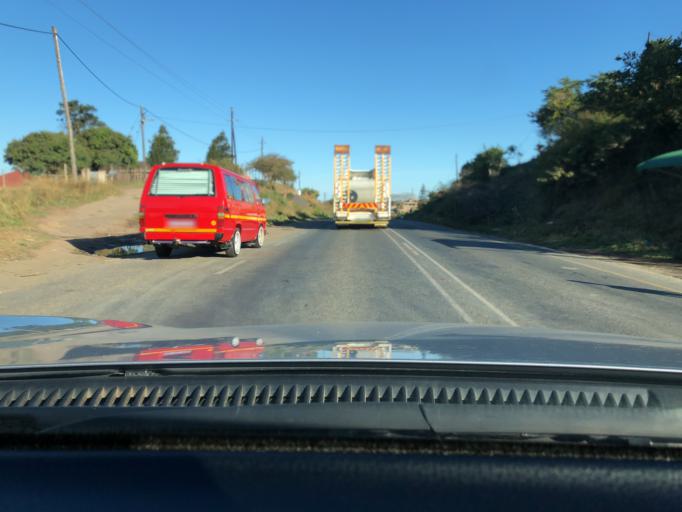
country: ZA
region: KwaZulu-Natal
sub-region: eThekwini Metropolitan Municipality
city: Umkomaas
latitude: -30.0163
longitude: 30.8082
